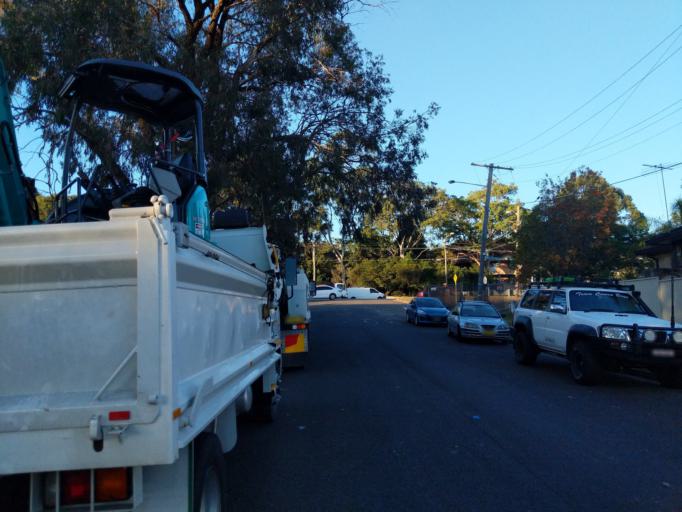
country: AU
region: New South Wales
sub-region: Sutherland Shire
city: Kirrawee
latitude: -34.0314
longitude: 151.0701
